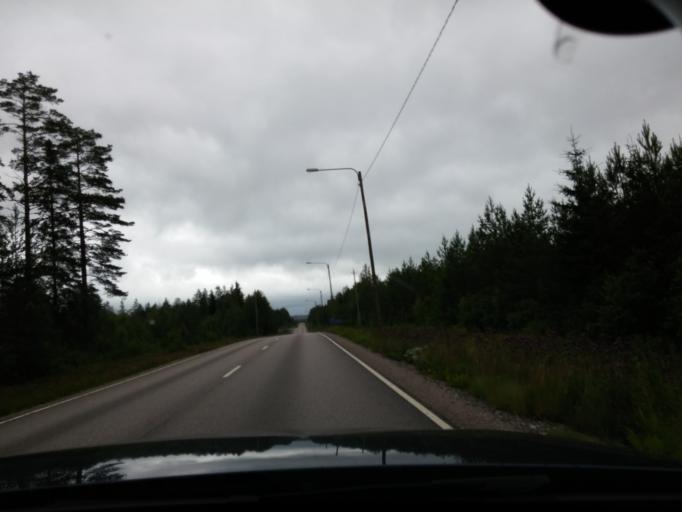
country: FI
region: Central Finland
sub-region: Saarijaervi-Viitasaari
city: Pylkoenmaeki
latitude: 62.6347
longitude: 24.8145
